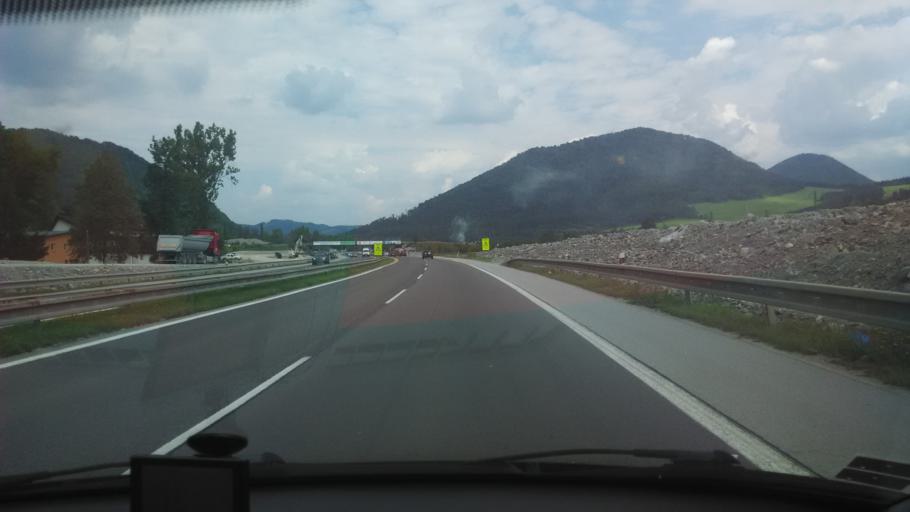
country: SK
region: Zilinsky
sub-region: Okres Zilina
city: Zilina
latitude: 49.2466
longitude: 18.7438
